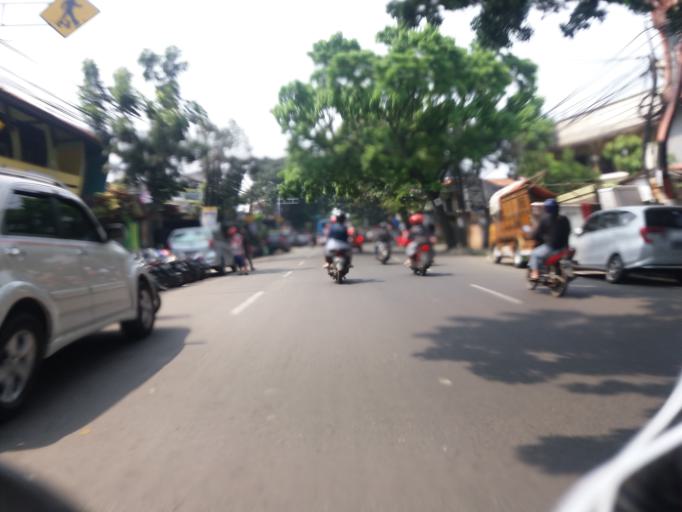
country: ID
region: West Java
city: Bandung
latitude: -6.9155
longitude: 107.5845
